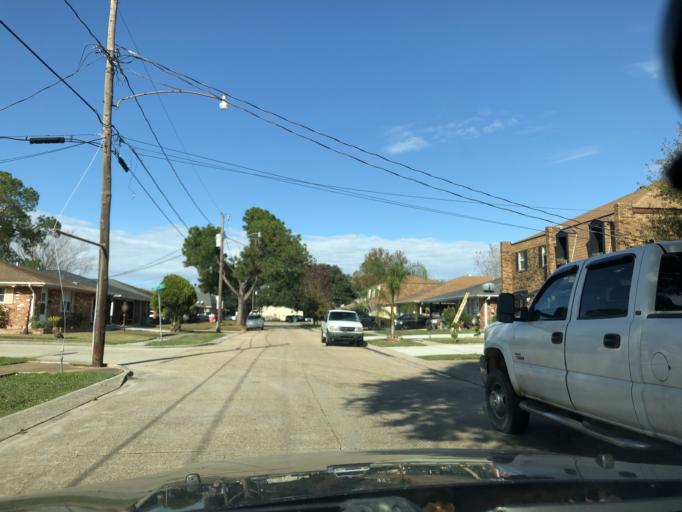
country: US
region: Louisiana
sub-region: Jefferson Parish
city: Metairie Terrace
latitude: 29.9956
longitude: -90.1673
